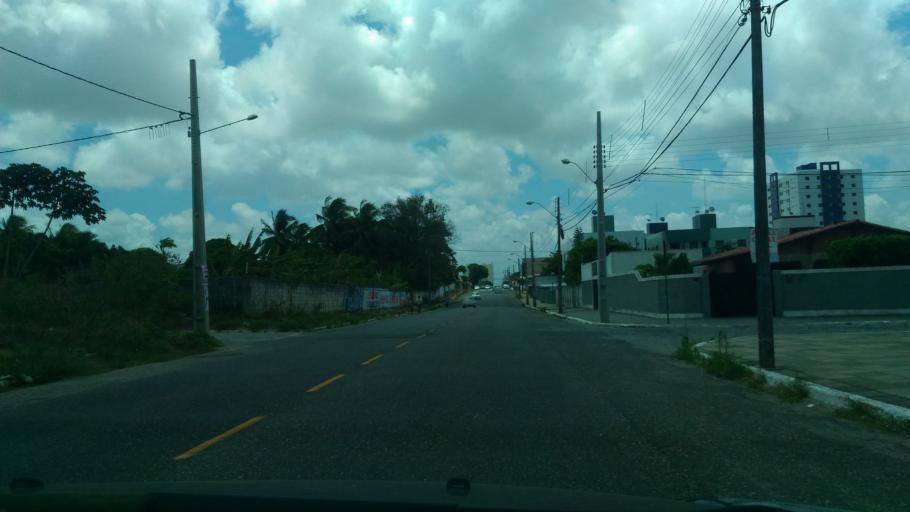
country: BR
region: Paraiba
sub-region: Joao Pessoa
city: Joao Pessoa
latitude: -7.1496
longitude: -34.8315
